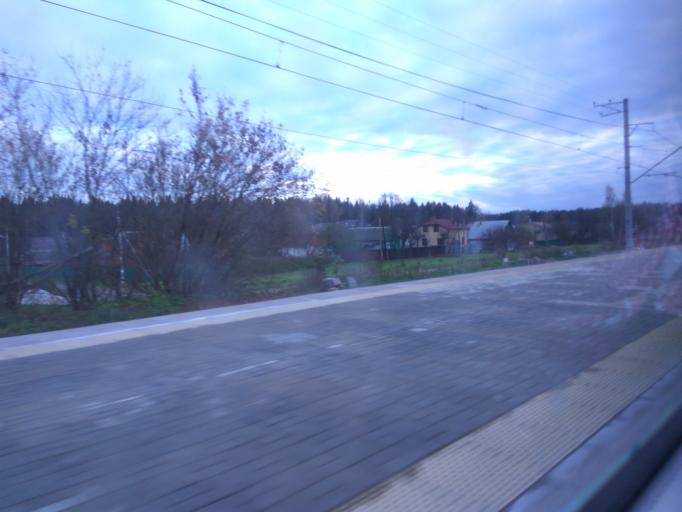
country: RU
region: Moskovskaya
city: Kievskij
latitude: 55.4793
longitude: 36.9155
